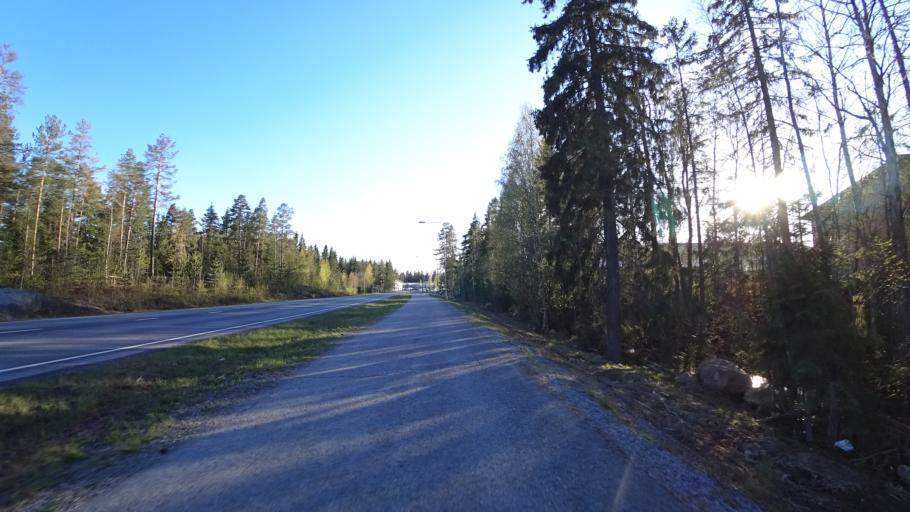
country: FI
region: Pirkanmaa
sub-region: Tampere
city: Nokia
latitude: 61.4959
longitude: 23.5491
